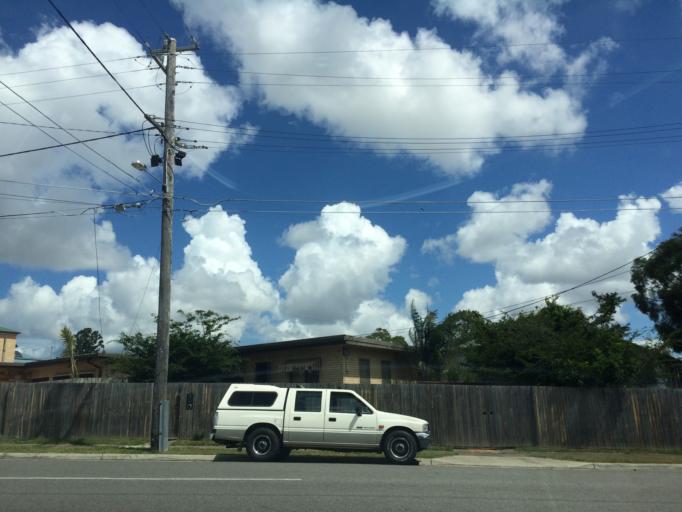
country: AU
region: Queensland
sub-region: Brisbane
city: Seven Hills
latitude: -27.4843
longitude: 153.0628
